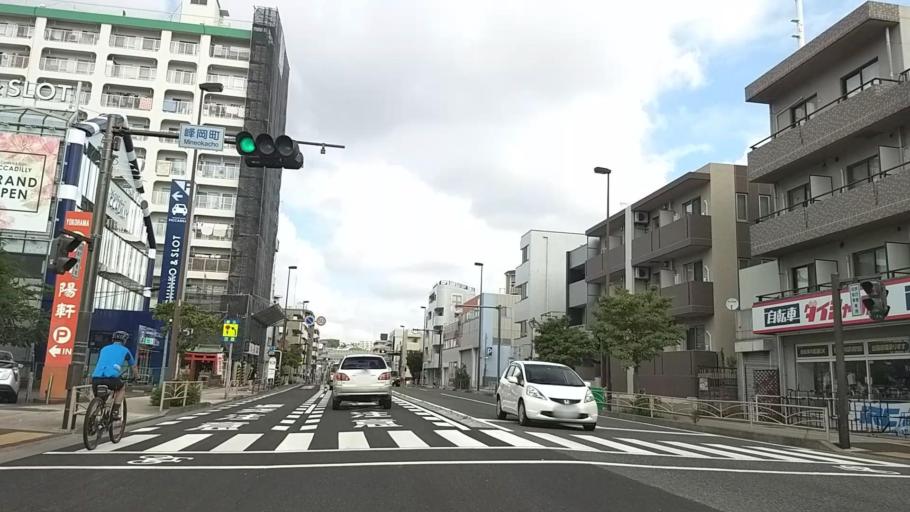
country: JP
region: Kanagawa
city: Yokohama
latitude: 35.4618
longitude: 139.5952
